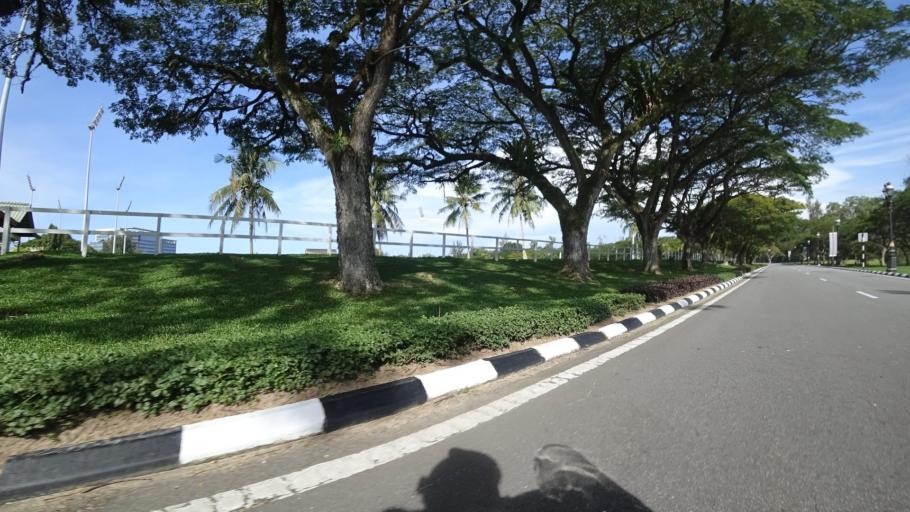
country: BN
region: Brunei and Muara
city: Bandar Seri Begawan
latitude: 4.9442
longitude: 114.8312
